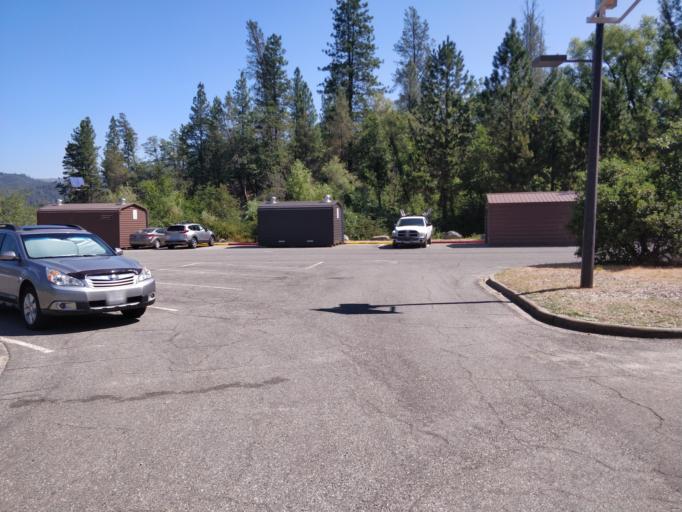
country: US
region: California
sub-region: Shasta County
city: Shasta
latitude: 40.6186
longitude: -122.5693
